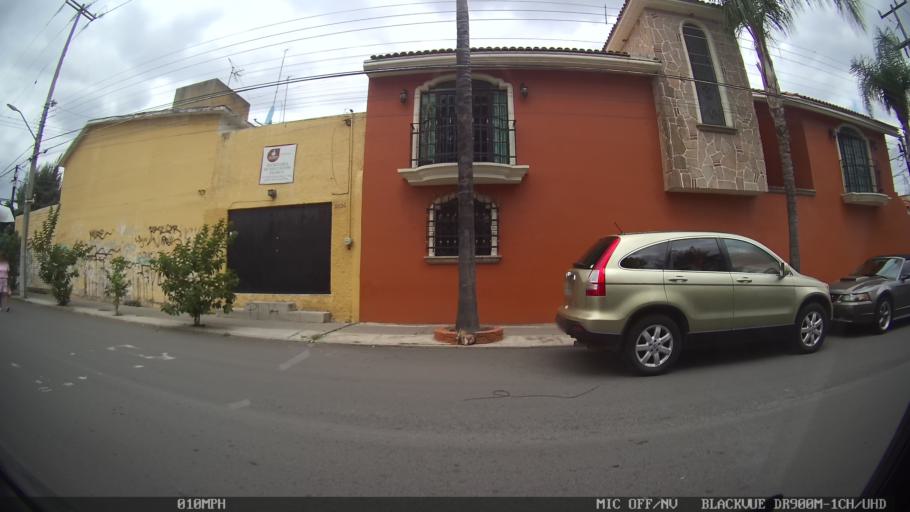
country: MX
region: Jalisco
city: Tonala
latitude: 20.6349
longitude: -103.2599
